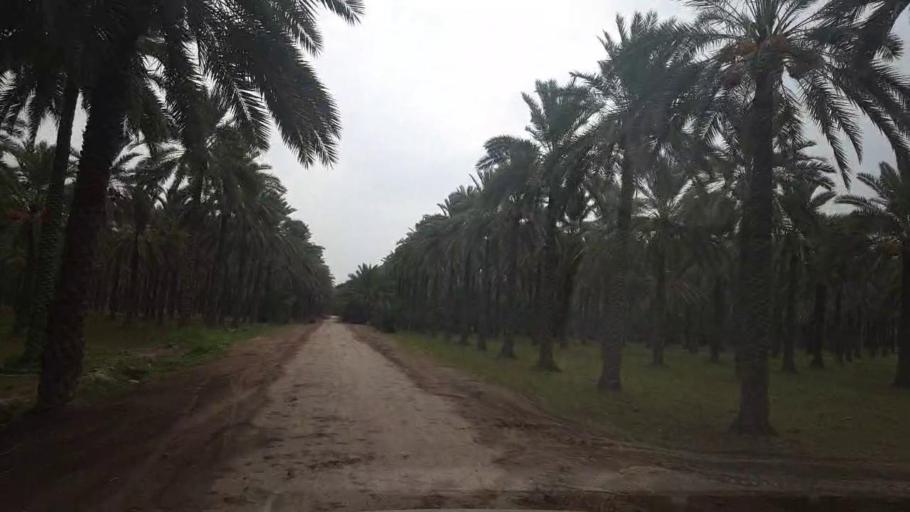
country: PK
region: Sindh
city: Khairpur
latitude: 27.6063
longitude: 68.8054
